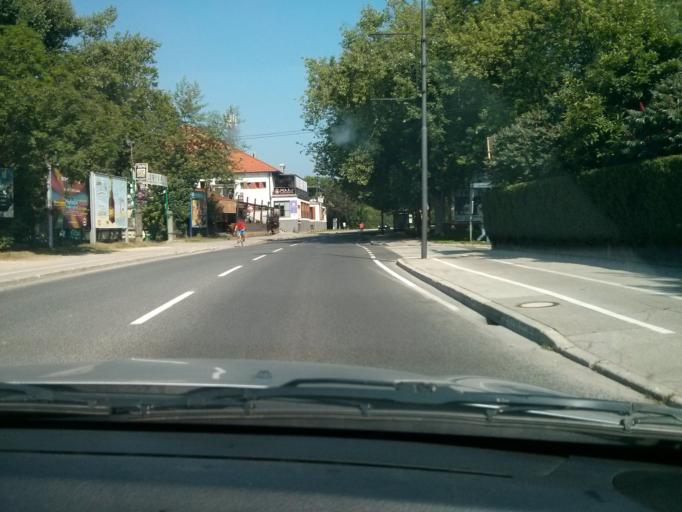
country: SI
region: Ljubljana
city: Ljubljana
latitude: 46.0707
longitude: 14.4790
